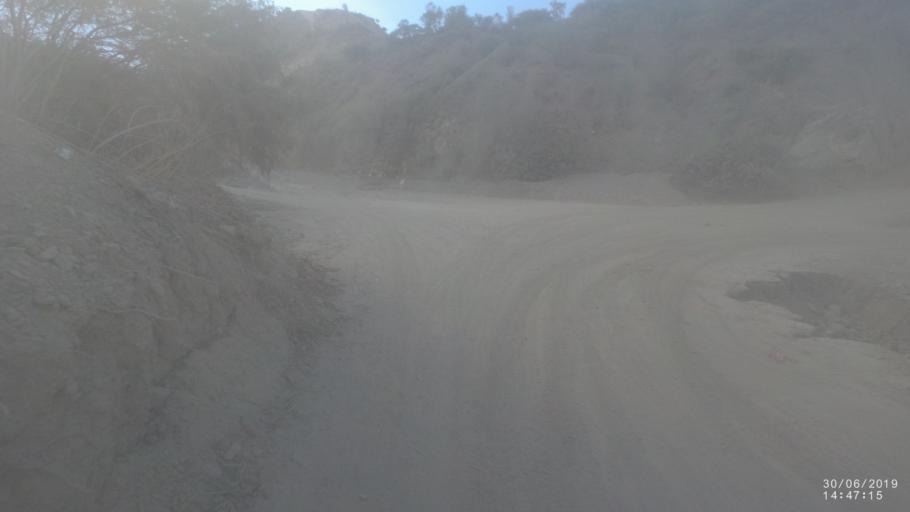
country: BO
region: Cochabamba
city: Irpa Irpa
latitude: -17.7929
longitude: -66.3471
